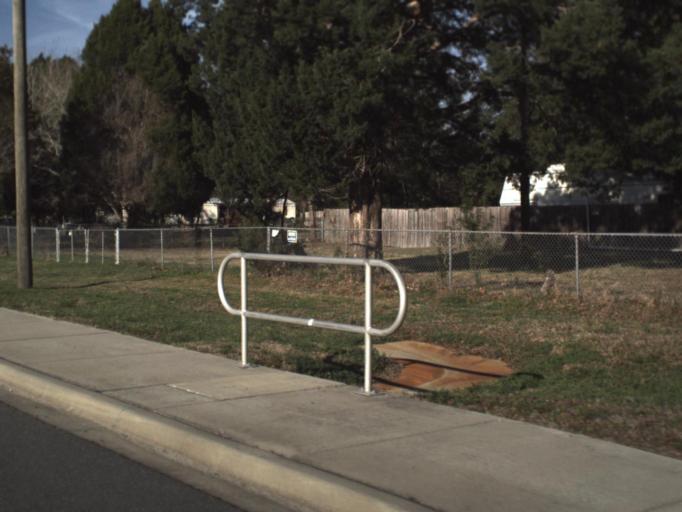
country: US
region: Florida
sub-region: Bay County
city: Laguna Beach
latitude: 30.3244
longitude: -85.8565
